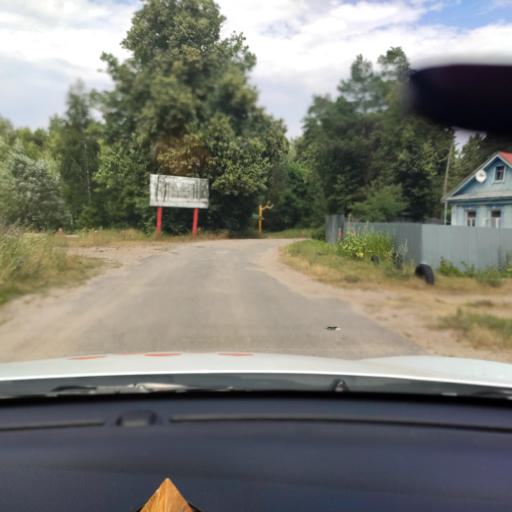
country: RU
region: Tatarstan
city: Osinovo
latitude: 55.9103
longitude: 48.9619
